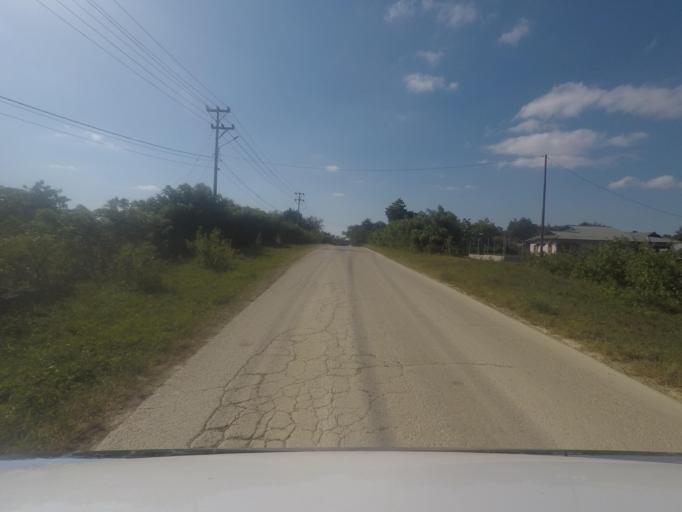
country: TL
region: Lautem
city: Lospalos
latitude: -8.4778
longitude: 126.9926
